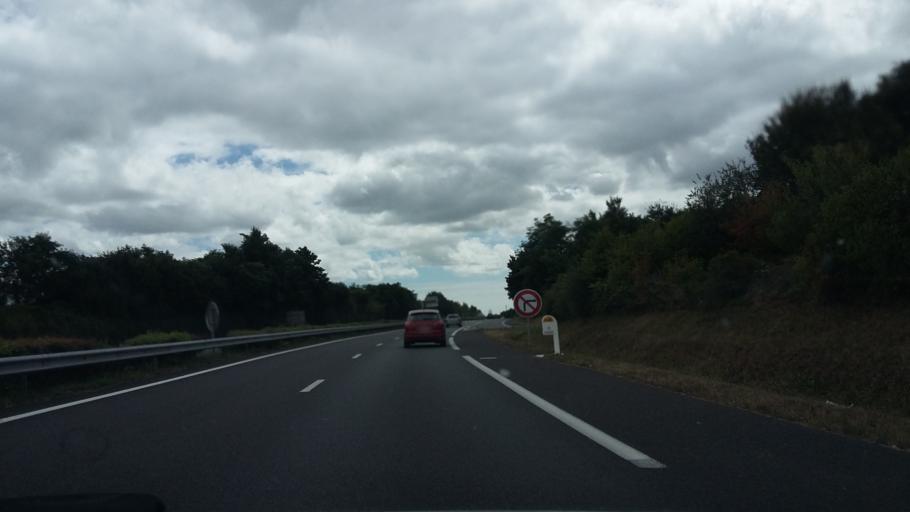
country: FR
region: Pays de la Loire
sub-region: Departement de la Vendee
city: Challans
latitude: 46.8510
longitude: -1.8508
